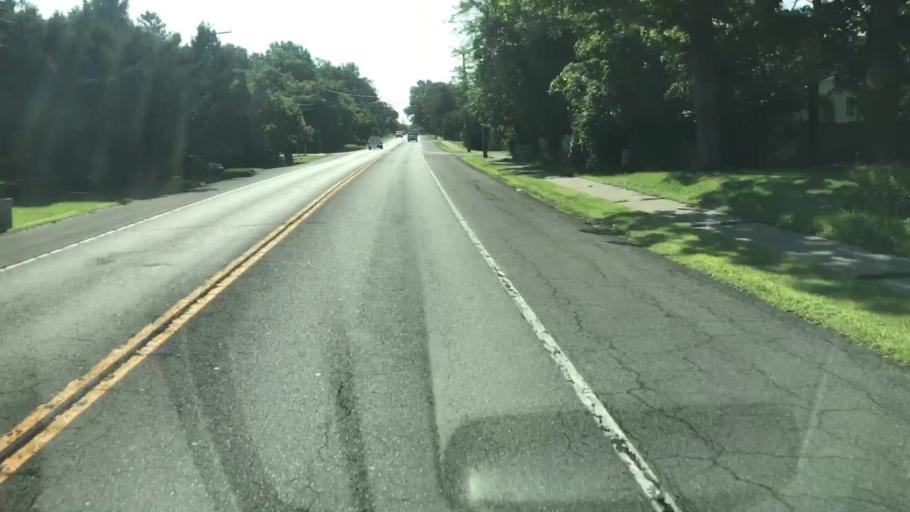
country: US
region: New York
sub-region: Onondaga County
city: Manlius
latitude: 43.0104
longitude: -75.9957
